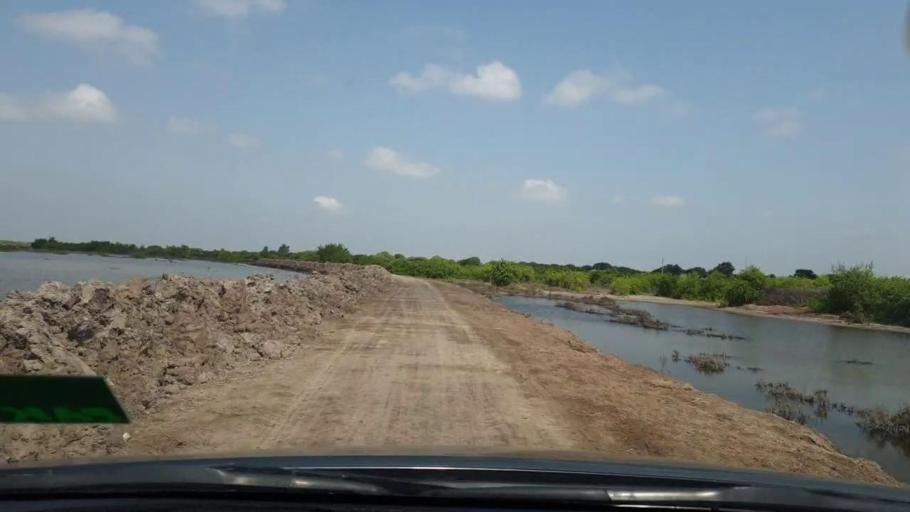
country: PK
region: Sindh
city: Tando Bago
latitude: 24.9534
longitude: 69.0760
